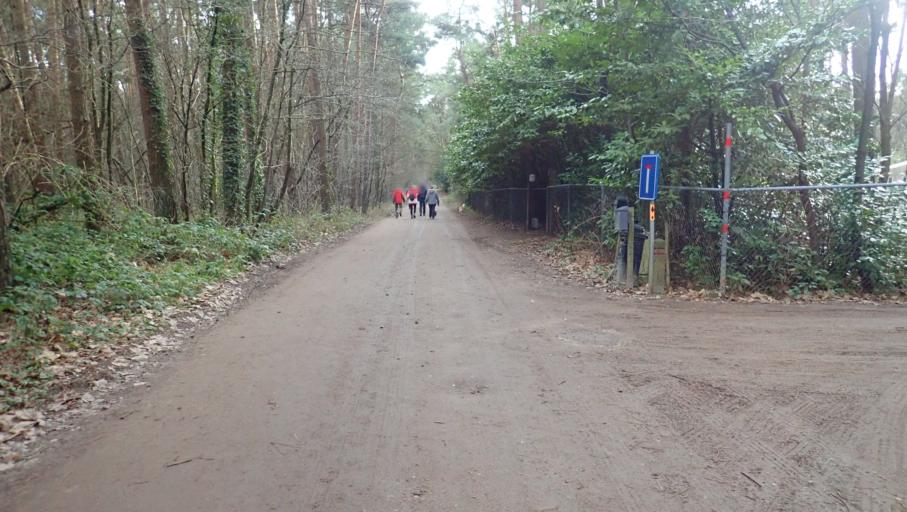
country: BE
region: Flanders
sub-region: Provincie Antwerpen
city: Lille
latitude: 51.2749
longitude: 4.8033
